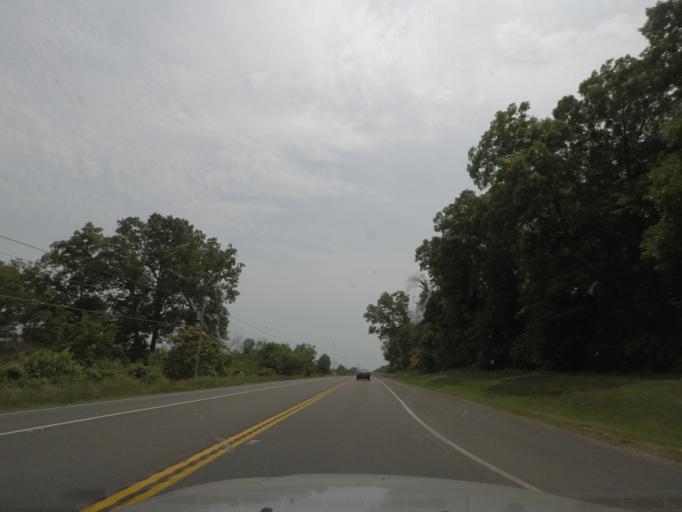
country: US
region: Virginia
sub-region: Prince William County
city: Bull Run Mountain Estates
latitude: 38.8776
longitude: -77.6343
